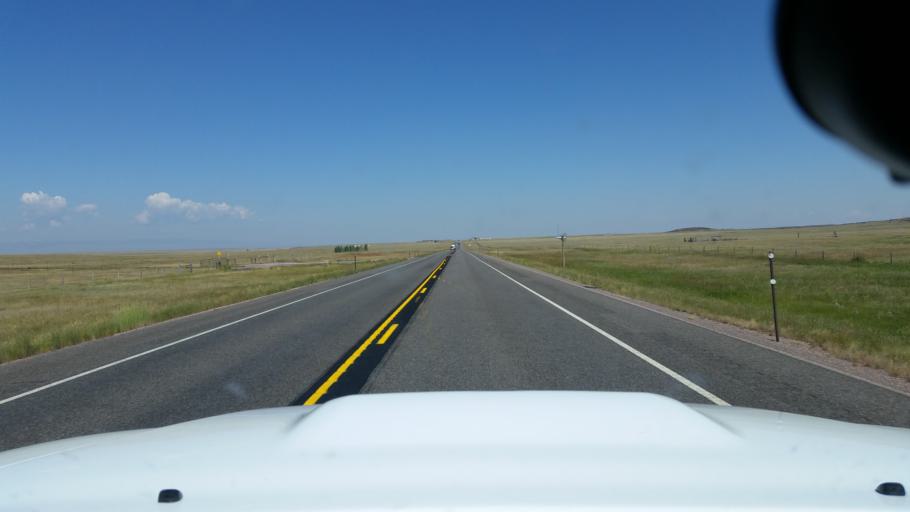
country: US
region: Wyoming
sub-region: Albany County
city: Laramie
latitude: 41.1038
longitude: -105.5298
